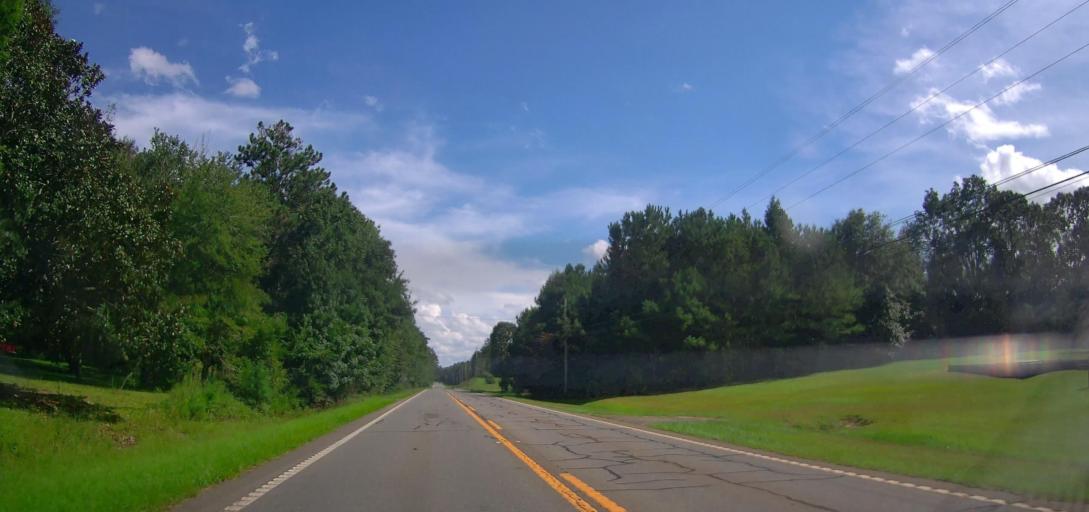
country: US
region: Georgia
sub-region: Talbot County
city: Sardis
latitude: 32.8117
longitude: -84.5982
